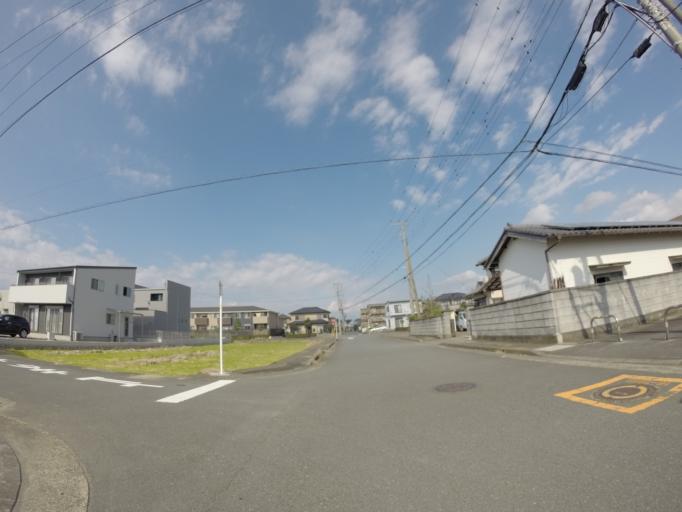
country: JP
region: Shizuoka
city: Fuji
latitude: 35.1327
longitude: 138.6636
